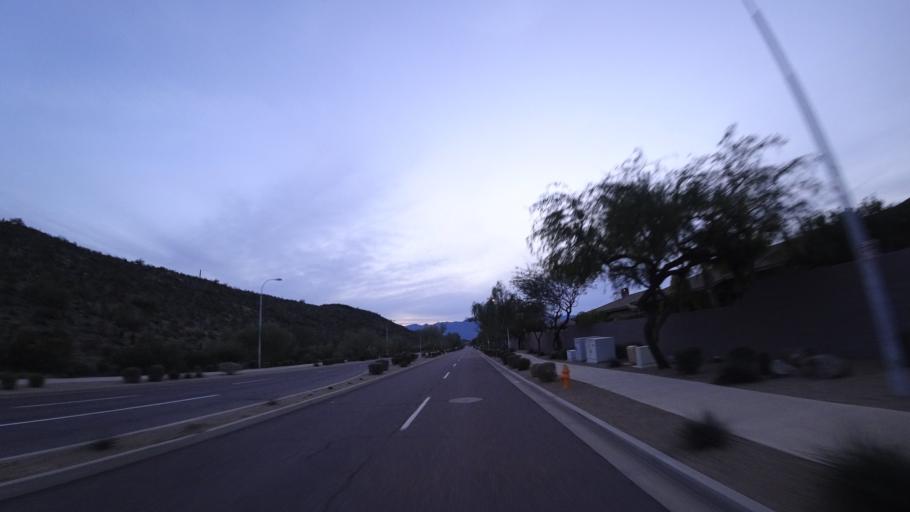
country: US
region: Arizona
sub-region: Maricopa County
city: Laveen
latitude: 33.3152
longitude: -112.0701
